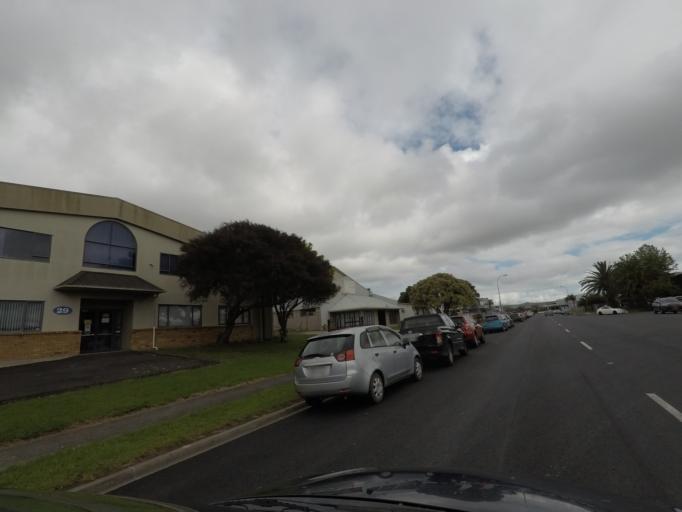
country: NZ
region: Auckland
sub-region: Auckland
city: Tamaki
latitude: -36.9311
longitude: 174.8845
